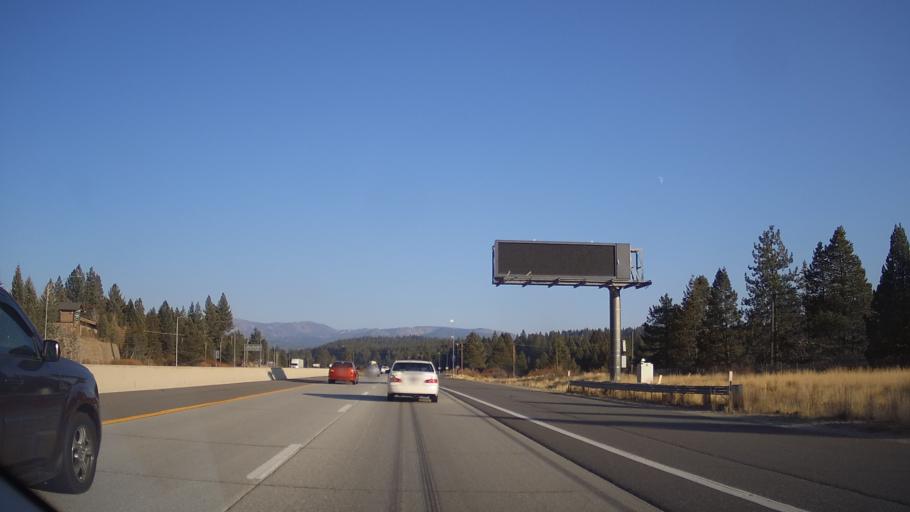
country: US
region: California
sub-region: Nevada County
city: Truckee
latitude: 39.3241
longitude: -120.2247
